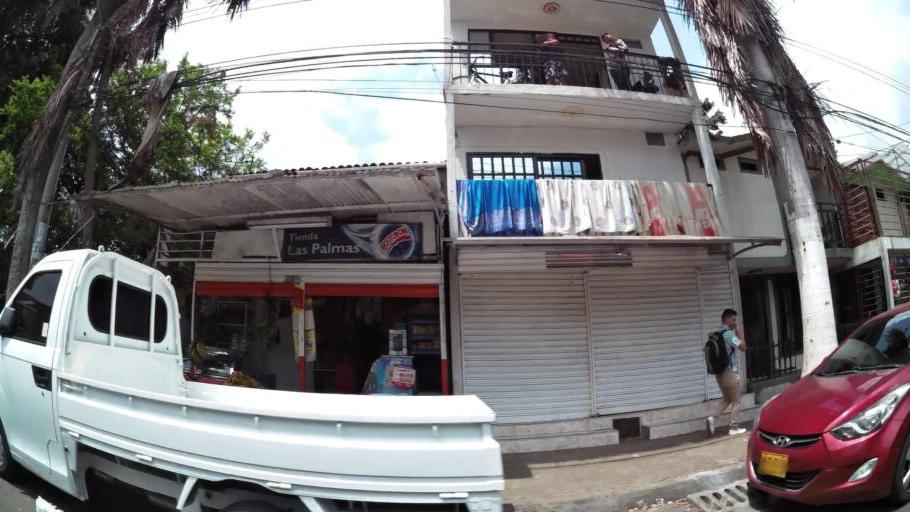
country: CO
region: Valle del Cauca
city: Cali
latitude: 3.4669
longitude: -76.4922
